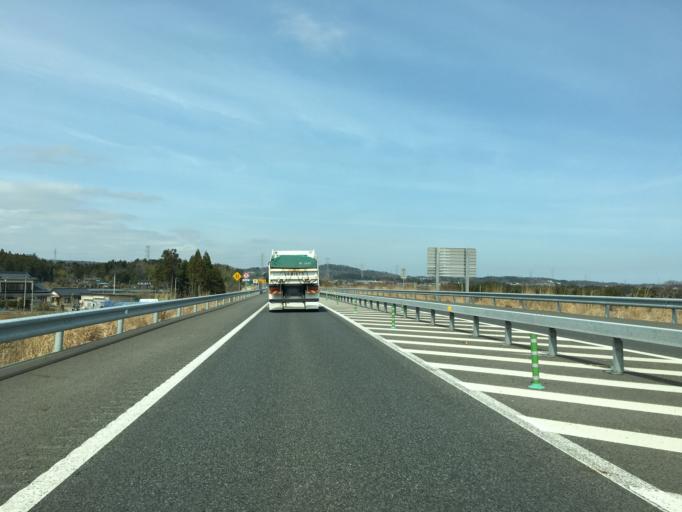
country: JP
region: Fukushima
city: Namie
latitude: 37.3860
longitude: 140.9674
